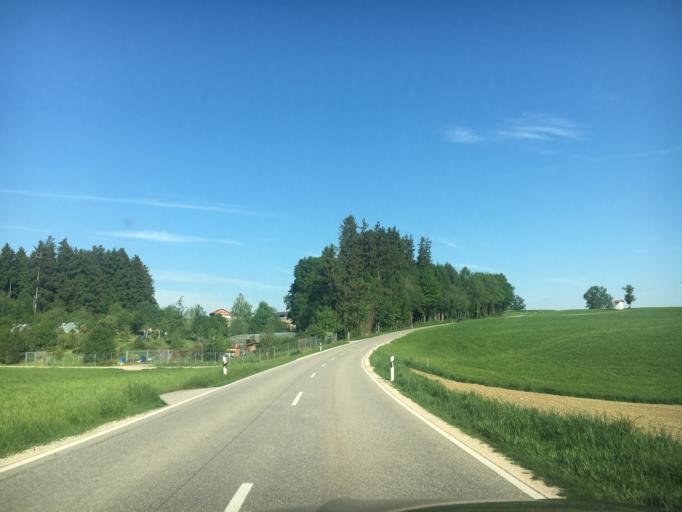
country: DE
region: Bavaria
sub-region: Upper Bavaria
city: Kirchweidach
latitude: 48.0680
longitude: 12.6064
